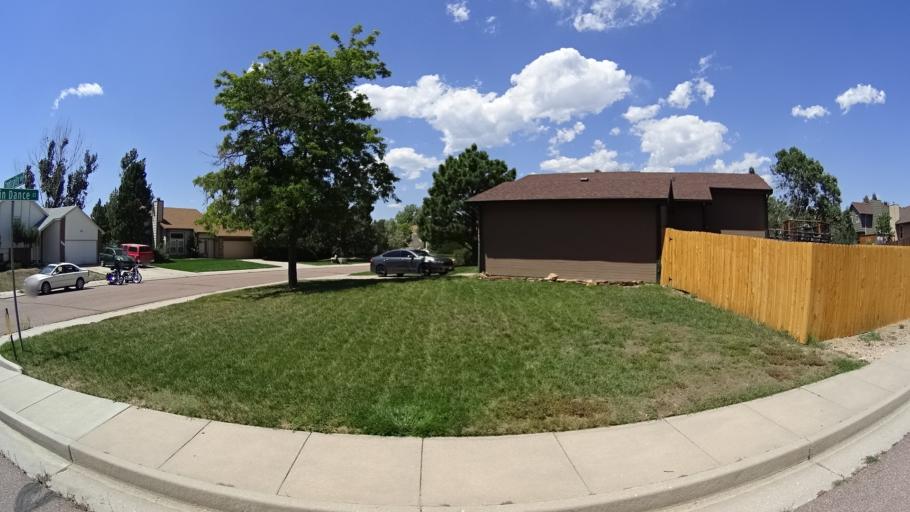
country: US
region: Colorado
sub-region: El Paso County
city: Black Forest
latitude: 38.9541
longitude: -104.7547
